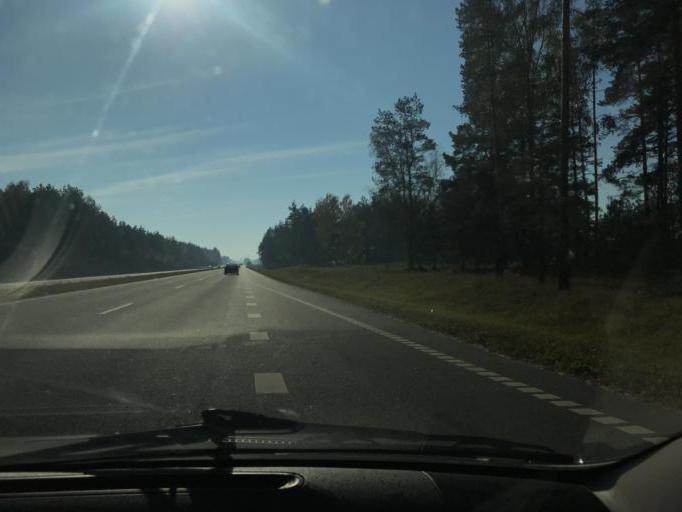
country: BY
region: Minsk
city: Slutsk
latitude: 53.3313
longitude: 27.5298
